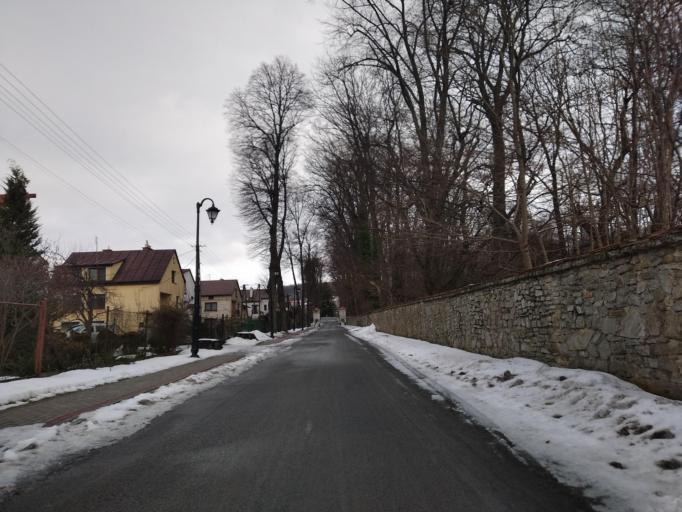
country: PL
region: Subcarpathian Voivodeship
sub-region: Powiat przemyski
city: Dubiecko
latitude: 49.8222
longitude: 22.3928
